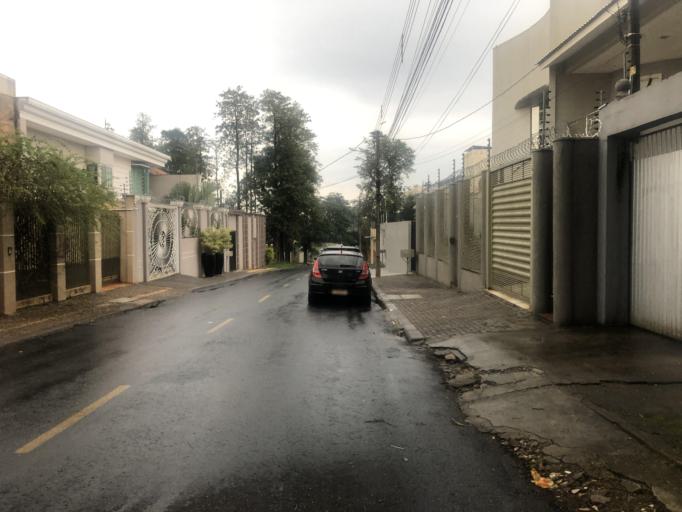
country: BR
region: Parana
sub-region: Foz Do Iguacu
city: Foz do Iguacu
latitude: -25.5188
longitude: -54.5804
